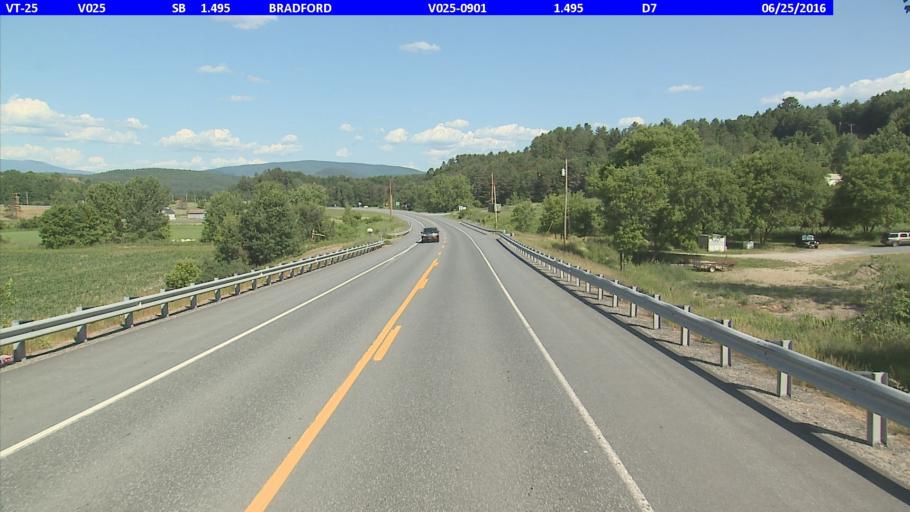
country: US
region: New Hampshire
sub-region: Grafton County
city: Orford
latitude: 43.9848
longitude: -72.1386
